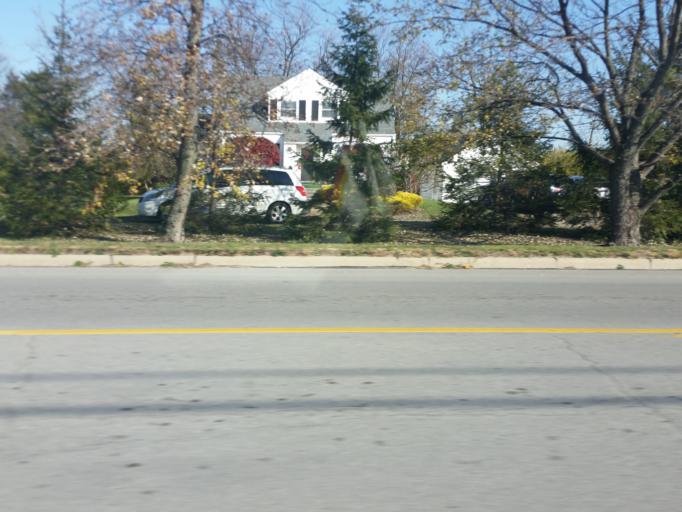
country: US
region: Ohio
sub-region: Butler County
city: Oxford
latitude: 39.4516
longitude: -84.6877
